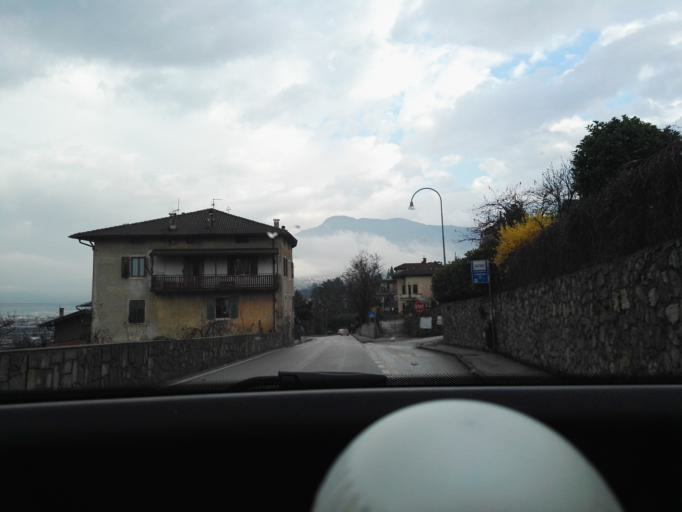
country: IT
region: Trentino-Alto Adige
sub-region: Provincia di Trento
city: Trento
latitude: 46.0494
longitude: 11.1373
